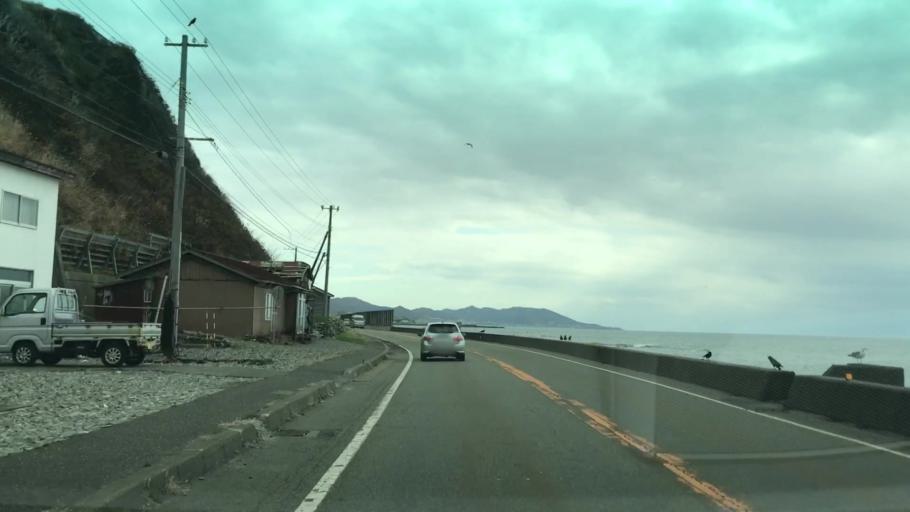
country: JP
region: Hokkaido
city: Shizunai-furukawacho
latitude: 42.0547
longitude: 143.0835
